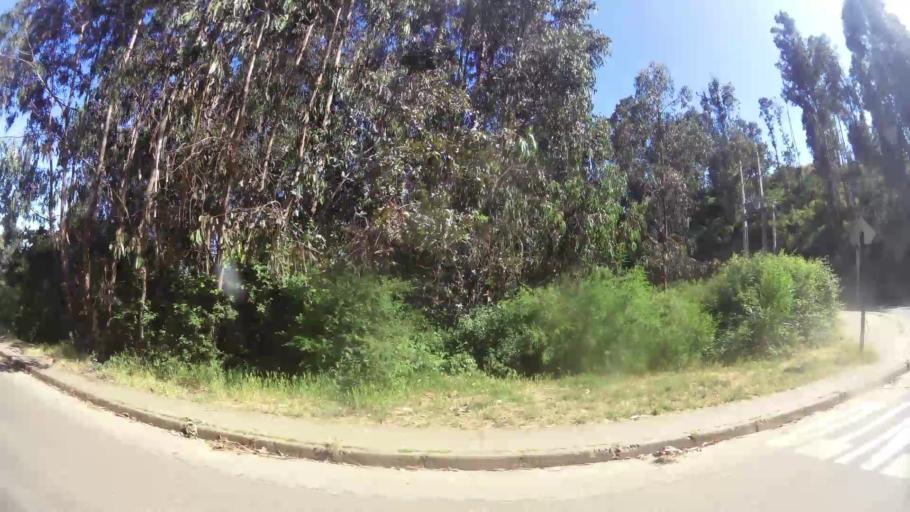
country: CL
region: Valparaiso
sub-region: Provincia de Valparaiso
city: Vina del Mar
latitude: -33.0629
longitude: -71.5776
